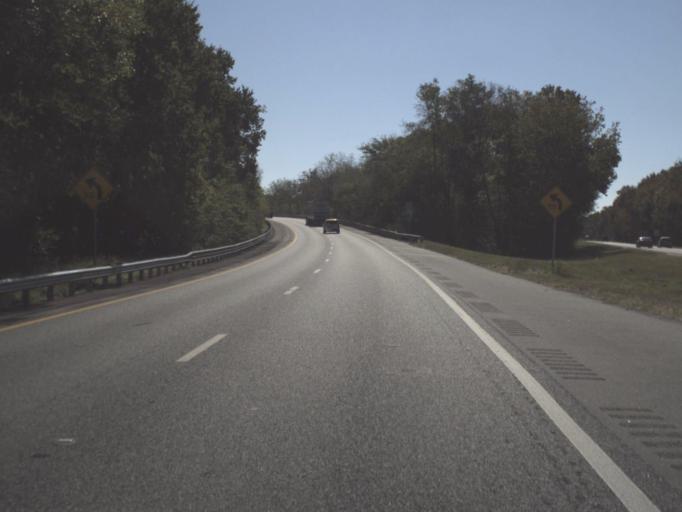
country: US
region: Florida
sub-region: Sumter County
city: Wildwood
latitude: 28.8600
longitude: -82.0916
